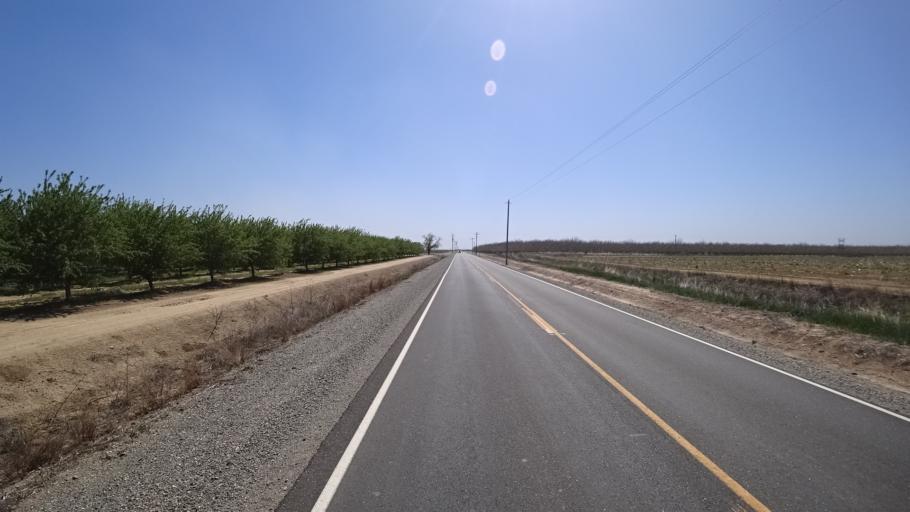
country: US
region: California
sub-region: Glenn County
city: Willows
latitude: 39.6125
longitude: -122.1376
